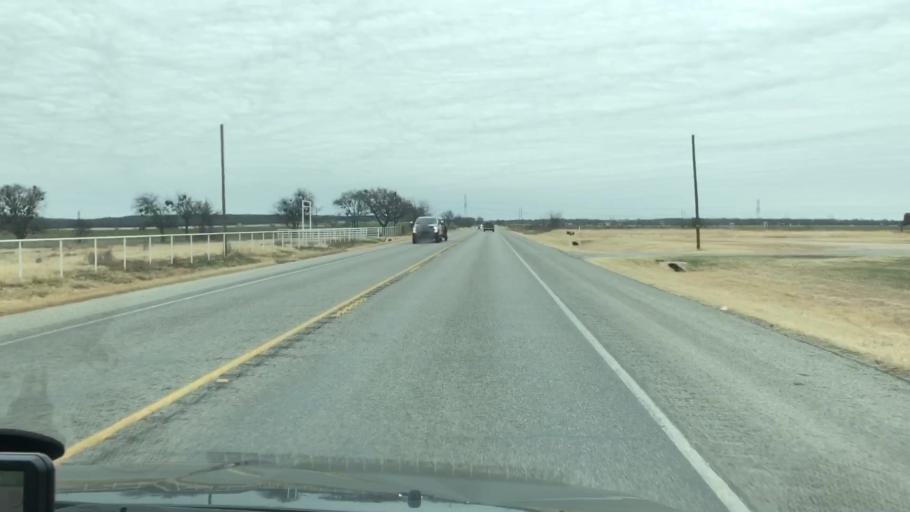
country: US
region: Texas
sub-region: Palo Pinto County
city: Mineral Wells
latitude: 32.9229
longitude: -98.0739
